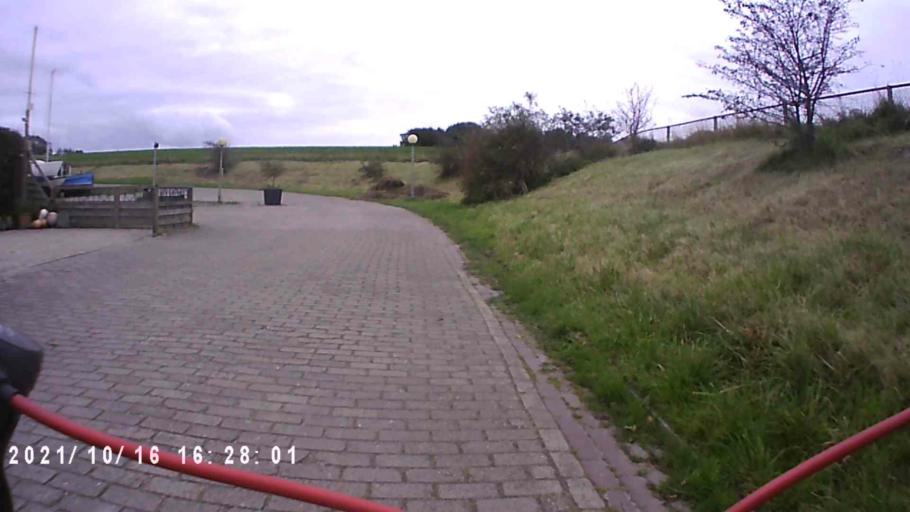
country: NL
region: Friesland
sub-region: Gemeente Dongeradeel
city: Anjum
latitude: 53.3827
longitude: 6.1551
